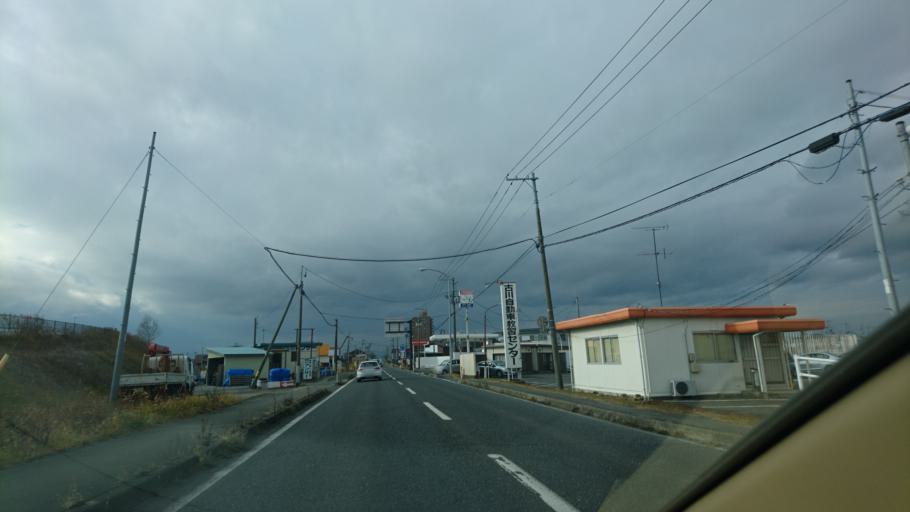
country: JP
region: Miyagi
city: Furukawa
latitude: 38.5690
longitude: 140.9889
